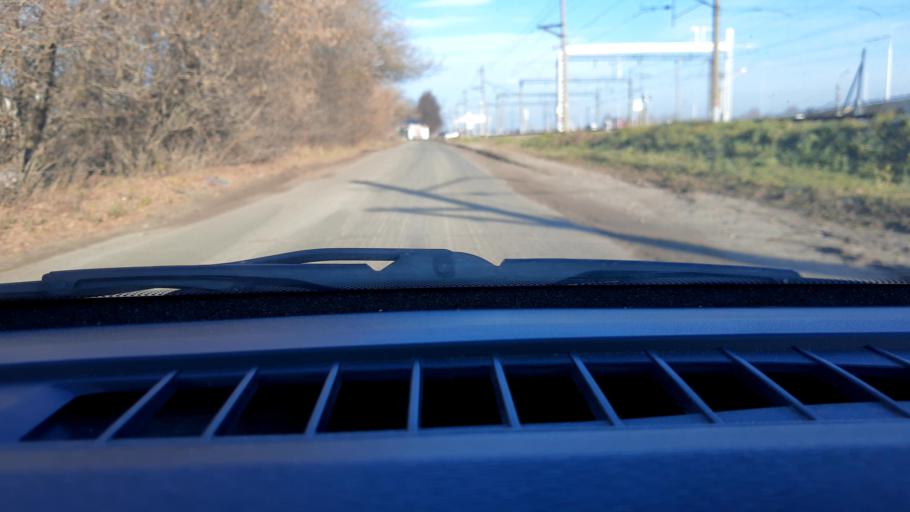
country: RU
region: Nizjnij Novgorod
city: Neklyudovo
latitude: 56.4030
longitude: 43.9815
